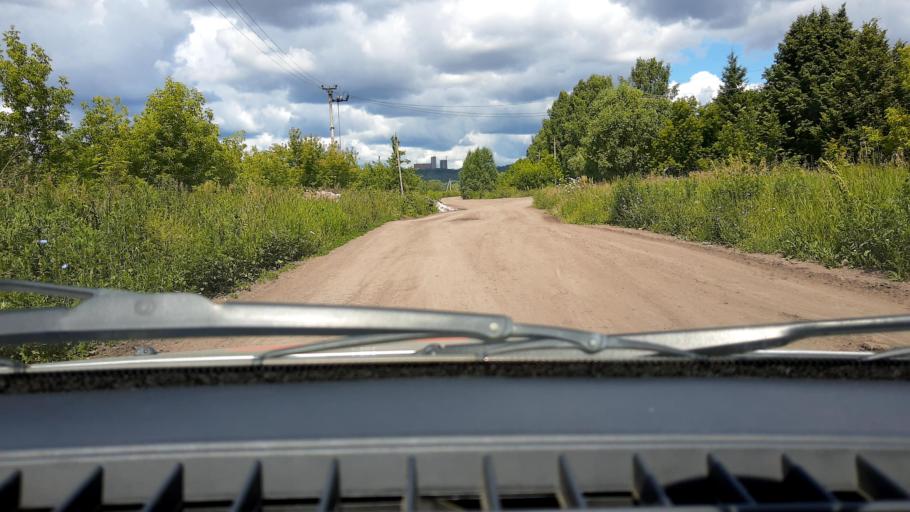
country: RU
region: Bashkortostan
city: Ufa
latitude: 54.6922
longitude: 56.0509
